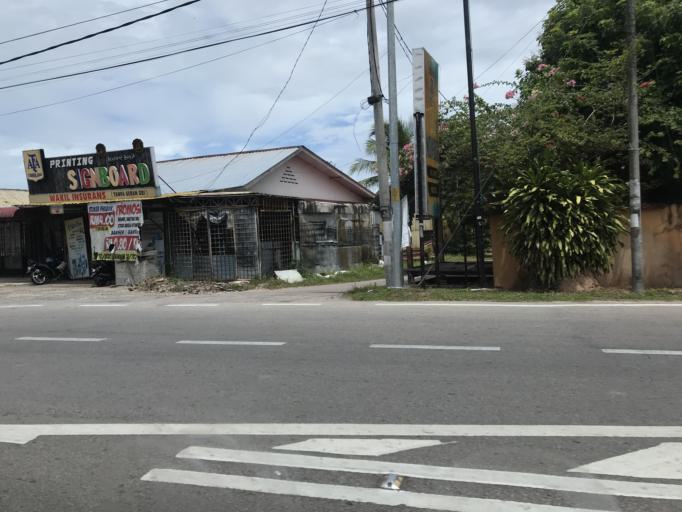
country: MY
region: Kelantan
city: Tumpat
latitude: 6.1716
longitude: 102.1871
